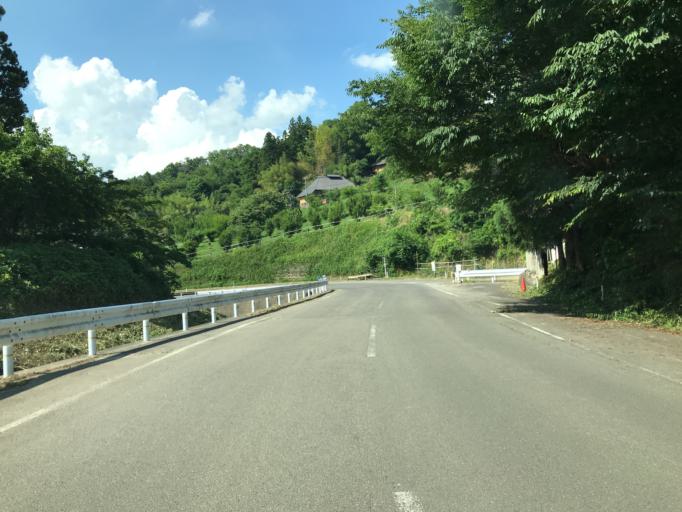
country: JP
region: Fukushima
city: Yanagawamachi-saiwaicho
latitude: 37.7917
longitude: 140.6485
